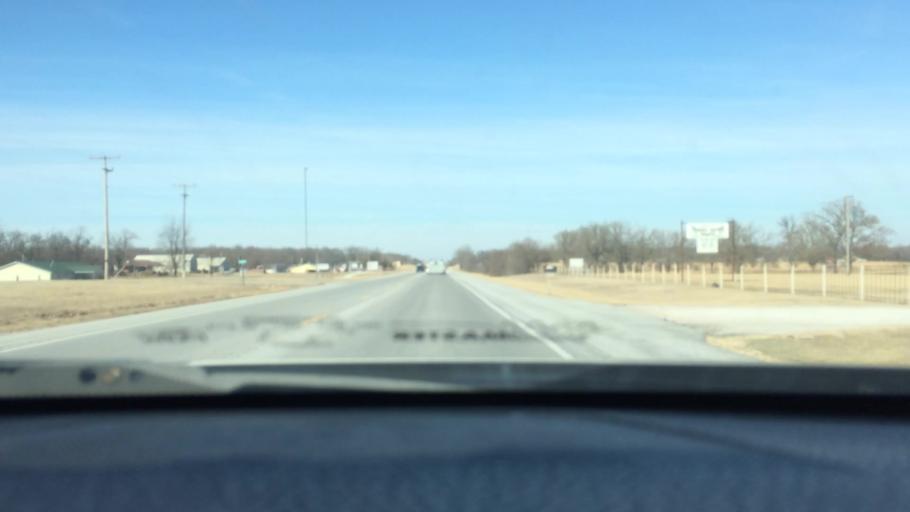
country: US
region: Missouri
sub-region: Newton County
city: Neosho
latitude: 36.8863
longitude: -94.3174
